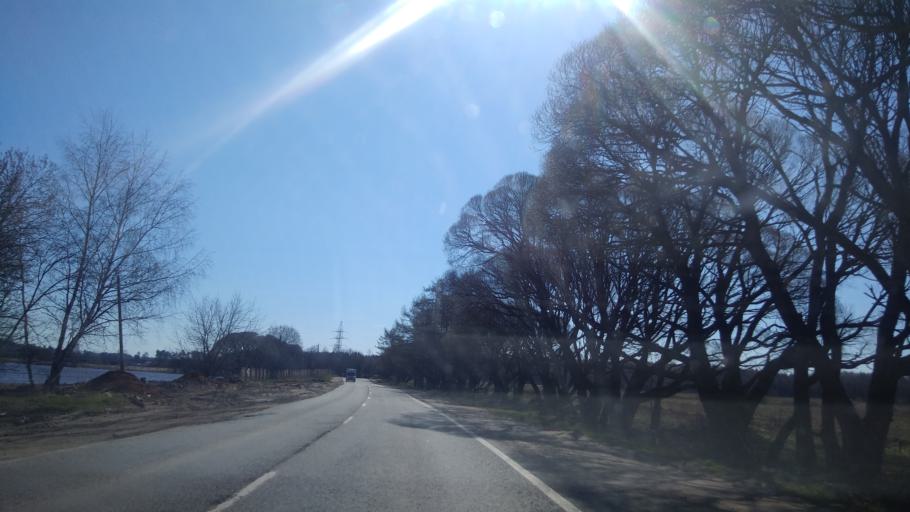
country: RU
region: Moskovskaya
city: Pravdinskiy
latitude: 56.0446
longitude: 37.8851
